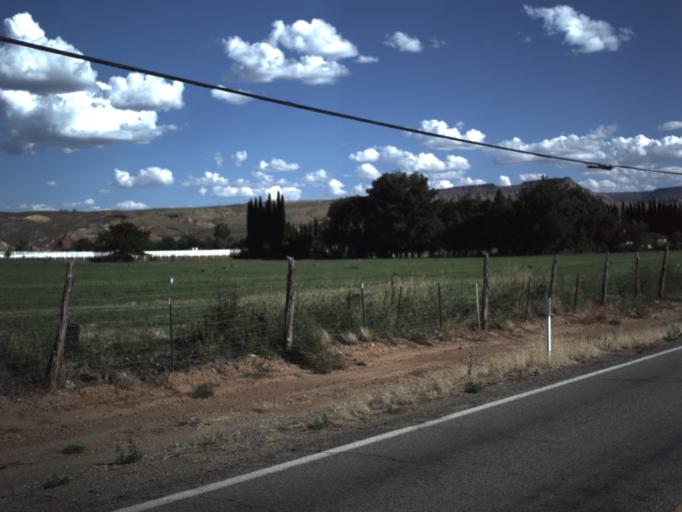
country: US
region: Utah
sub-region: Washington County
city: Toquerville
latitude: 37.2375
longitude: -113.2810
